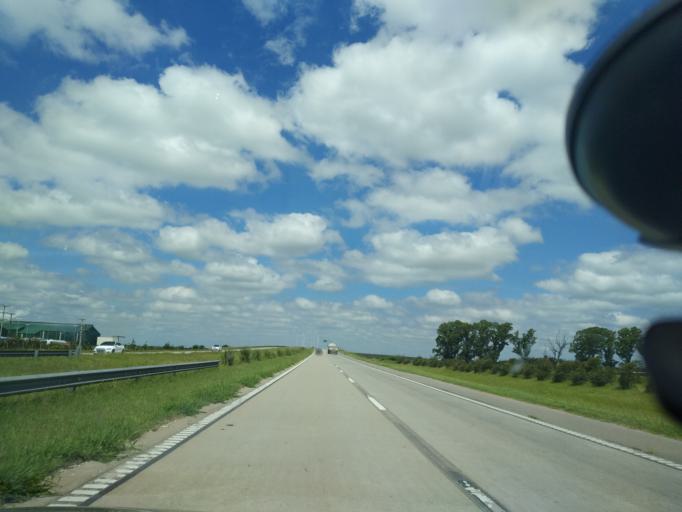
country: AR
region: Cordoba
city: Villa Maria
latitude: -32.4166
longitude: -63.1632
